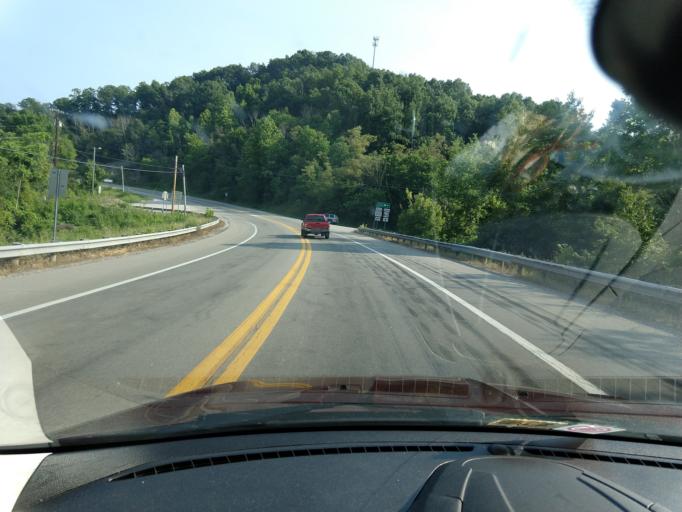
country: US
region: West Virginia
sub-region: Jackson County
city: Ravenswood
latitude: 38.8666
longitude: -81.8177
